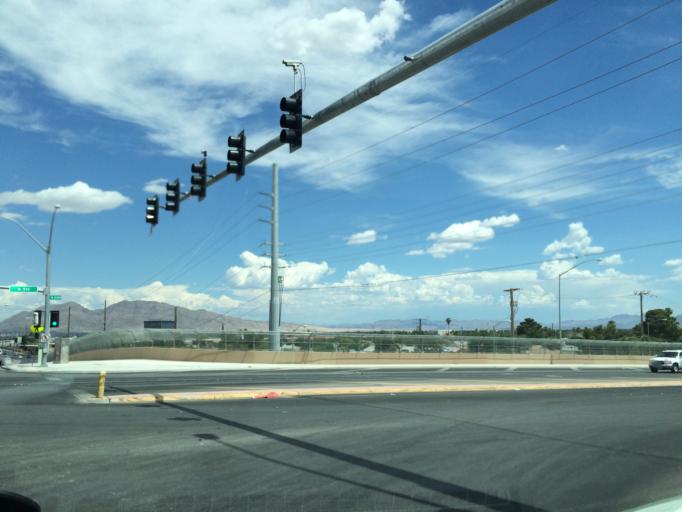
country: US
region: Nevada
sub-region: Clark County
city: North Las Vegas
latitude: 36.2033
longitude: -115.1339
